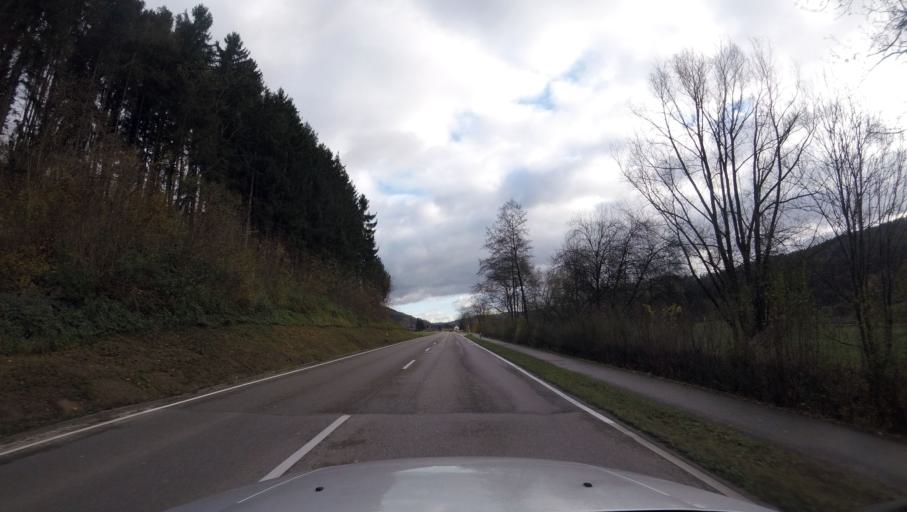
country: DE
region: Baden-Wuerttemberg
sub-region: Regierungsbezirk Stuttgart
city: Sulzbach an der Murr
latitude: 48.9989
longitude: 9.5240
